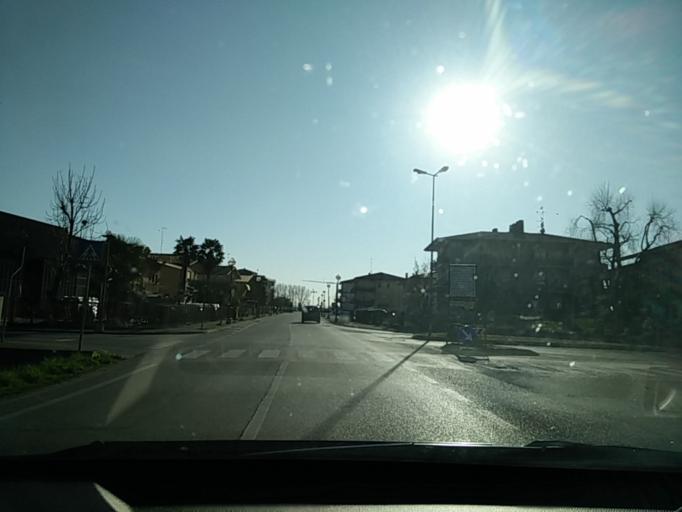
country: IT
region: Veneto
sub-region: Provincia di Treviso
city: Fontanelle
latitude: 45.8329
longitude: 12.4696
